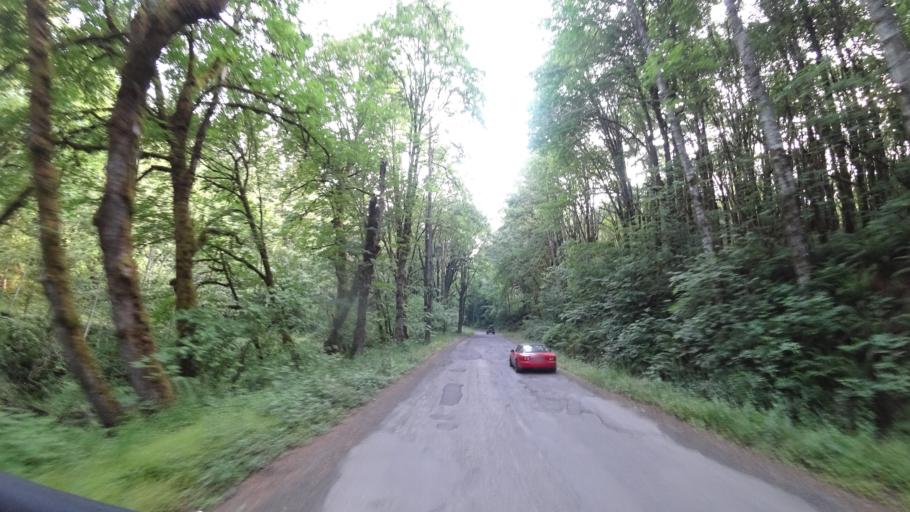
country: US
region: Oregon
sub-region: Clackamas County
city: Happy Valley
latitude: 45.4506
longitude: -122.5022
